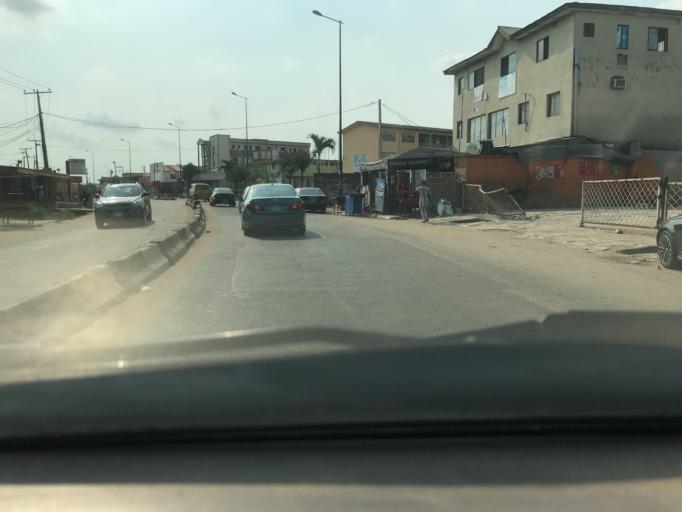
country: NG
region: Lagos
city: Agege
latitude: 6.6004
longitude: 3.2967
